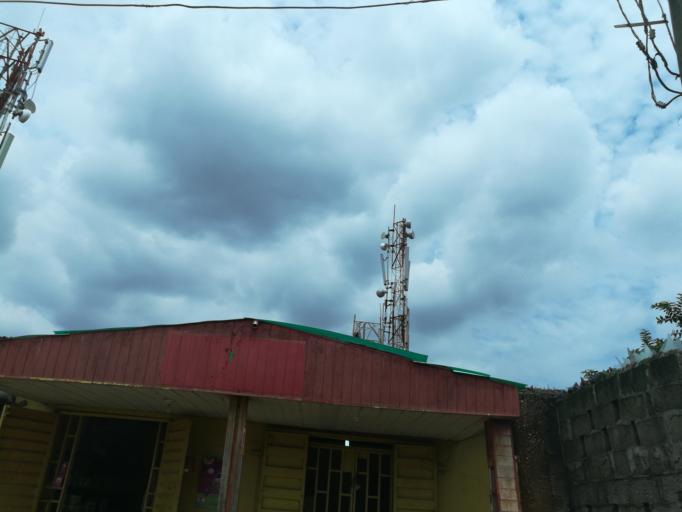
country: NG
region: Lagos
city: Oshodi
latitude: 6.5610
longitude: 3.3312
